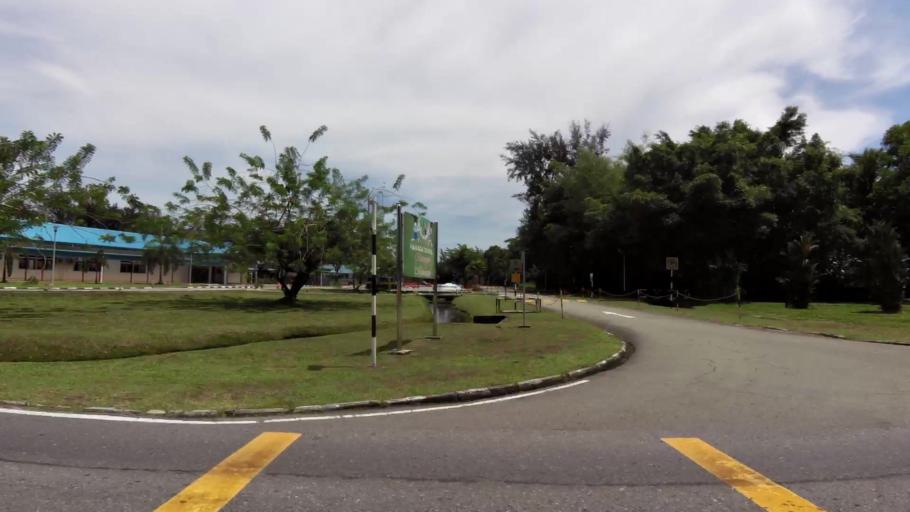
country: BN
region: Belait
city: Kuala Belait
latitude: 4.6013
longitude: 114.2754
